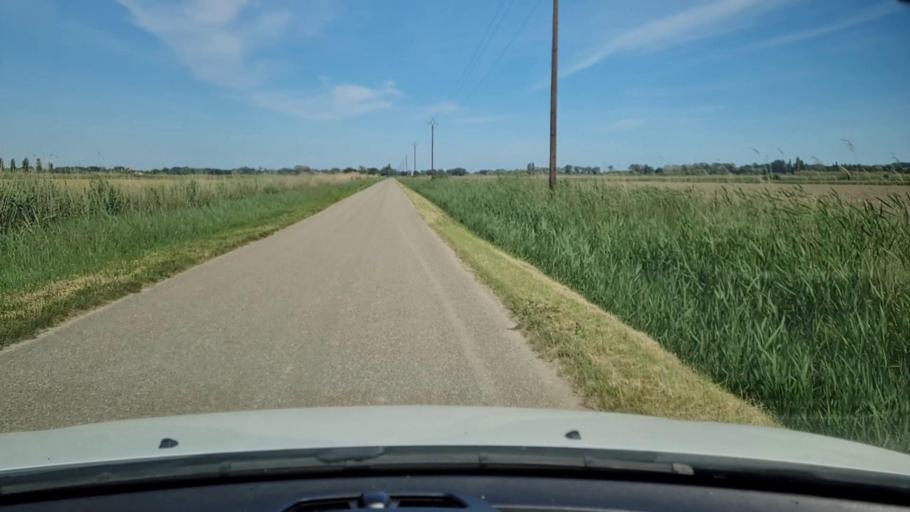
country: FR
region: Languedoc-Roussillon
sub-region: Departement du Gard
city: Saint-Gilles
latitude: 43.6031
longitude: 4.4503
